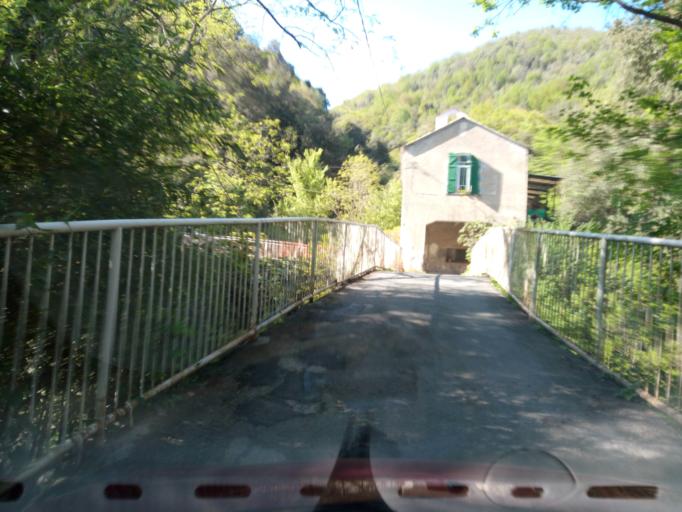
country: IT
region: Liguria
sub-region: Provincia di Genova
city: Sciarborasca
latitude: 44.3968
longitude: 8.5869
